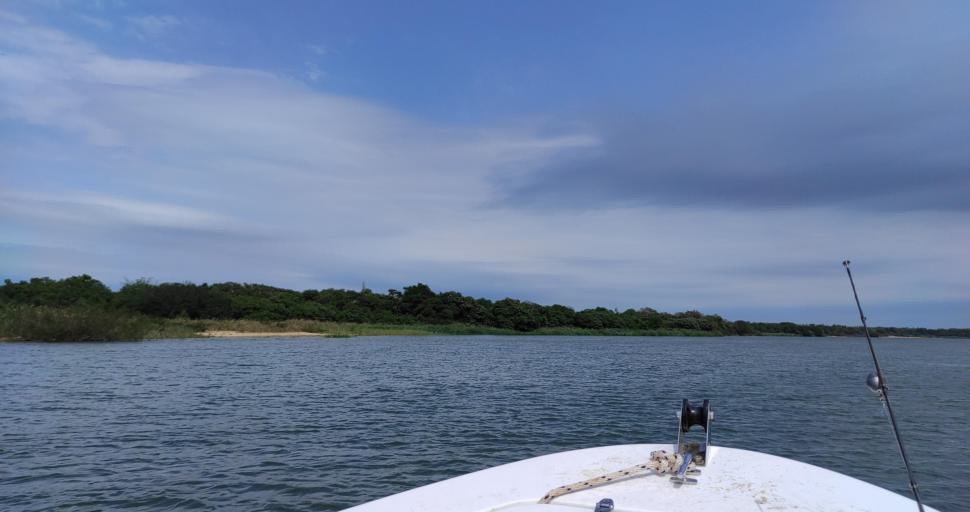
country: PY
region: Neembucu
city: Cerrito
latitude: -27.3460
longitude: -57.6892
